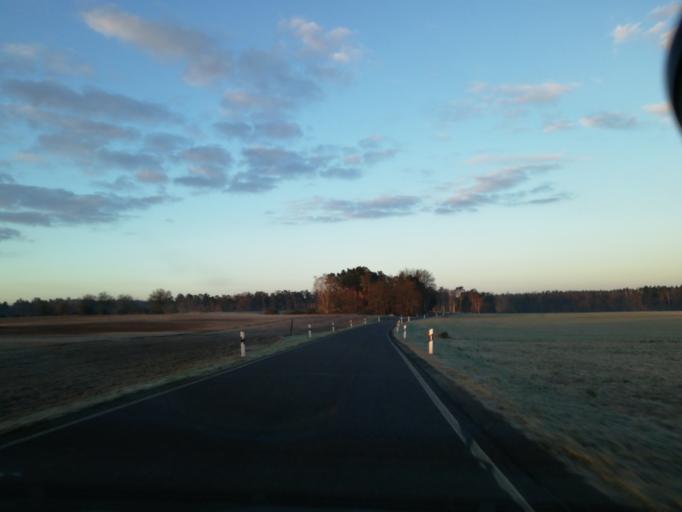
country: DE
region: Brandenburg
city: Calau
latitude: 51.7288
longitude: 13.9029
